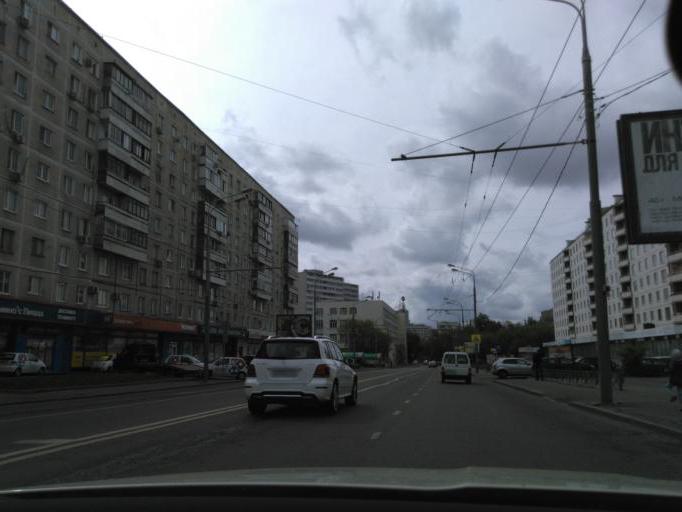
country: RU
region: Moscow
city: Mar'ina Roshcha
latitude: 55.7836
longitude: 37.6419
